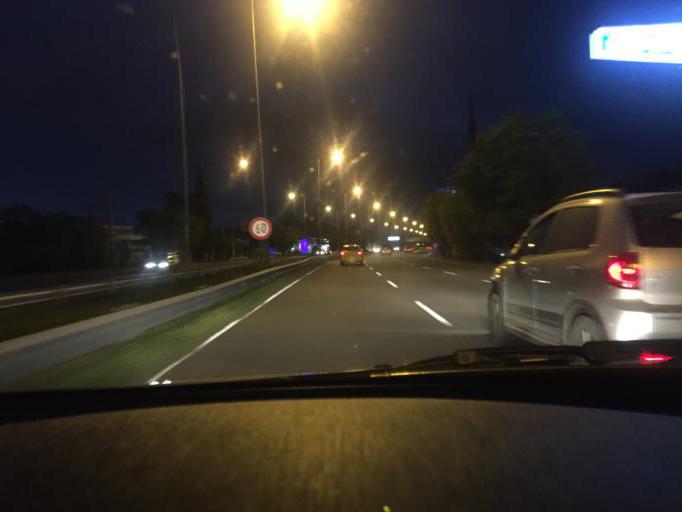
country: AR
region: Cordoba
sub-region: Departamento de Capital
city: Cordoba
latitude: -31.3327
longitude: -64.2096
